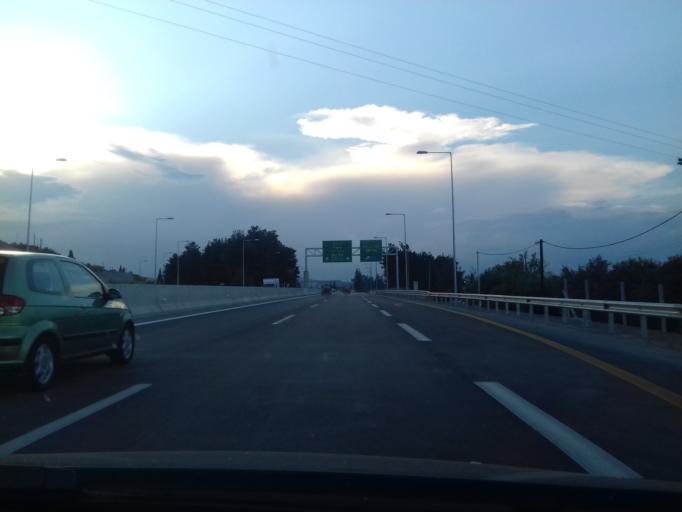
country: GR
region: West Greece
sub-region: Nomos Achaias
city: Temeni
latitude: 38.2190
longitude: 22.1068
